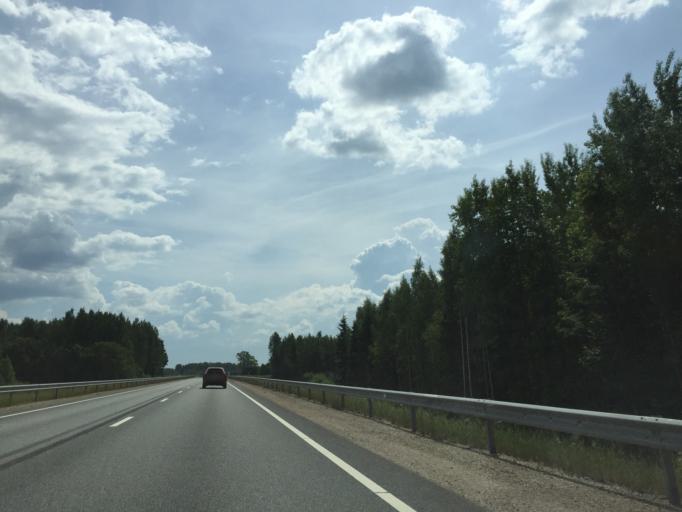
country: LV
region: Skriveri
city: Skriveri
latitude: 56.7504
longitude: 25.1201
